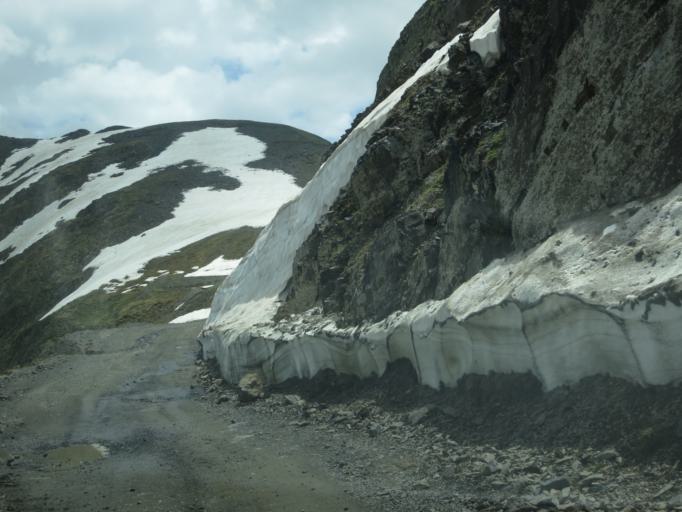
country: GE
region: Kakheti
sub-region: Telavi
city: Telavi
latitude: 42.2786
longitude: 45.5072
